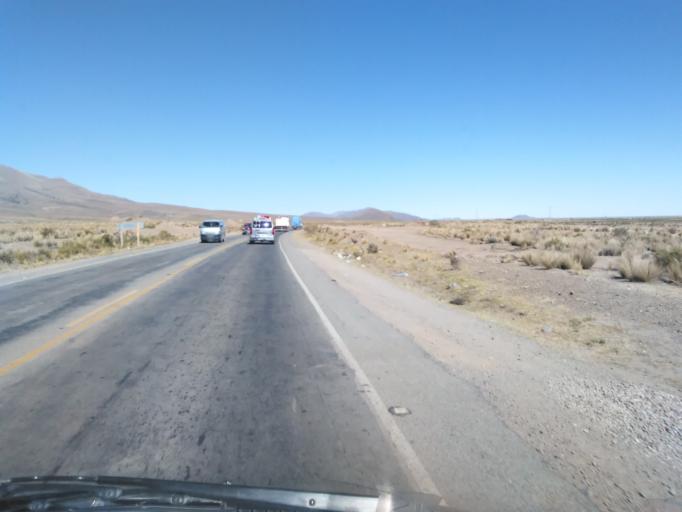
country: BO
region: Oruro
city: Machacamarca
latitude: -18.0578
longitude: -67.0065
